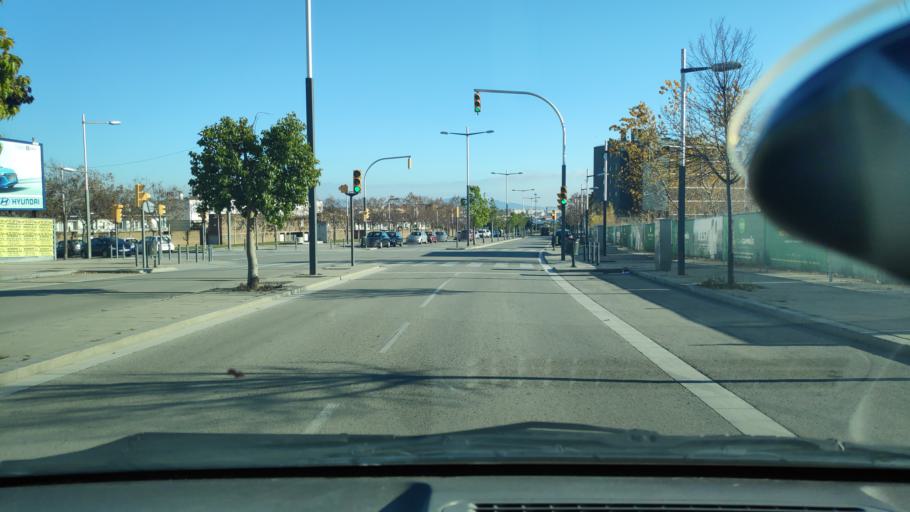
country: ES
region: Catalonia
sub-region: Provincia de Barcelona
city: Sant Quirze del Valles
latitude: 41.5410
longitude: 2.0878
